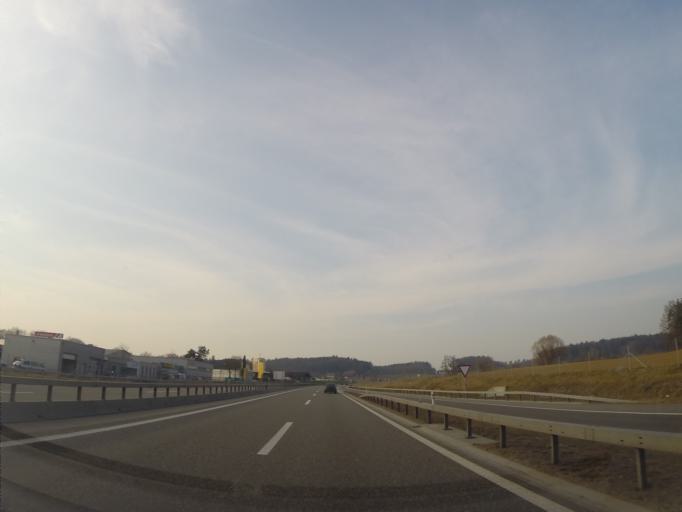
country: CH
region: Zurich
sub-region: Bezirk Andelfingen
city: Kleinandelfingen
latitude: 47.6041
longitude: 8.6897
